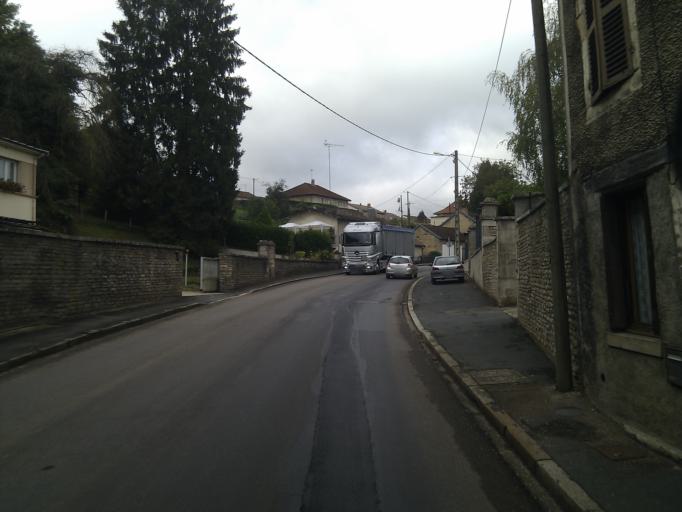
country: FR
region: Champagne-Ardenne
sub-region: Departement de la Haute-Marne
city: Doulaincourt-Saucourt
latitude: 48.2477
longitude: 5.3288
